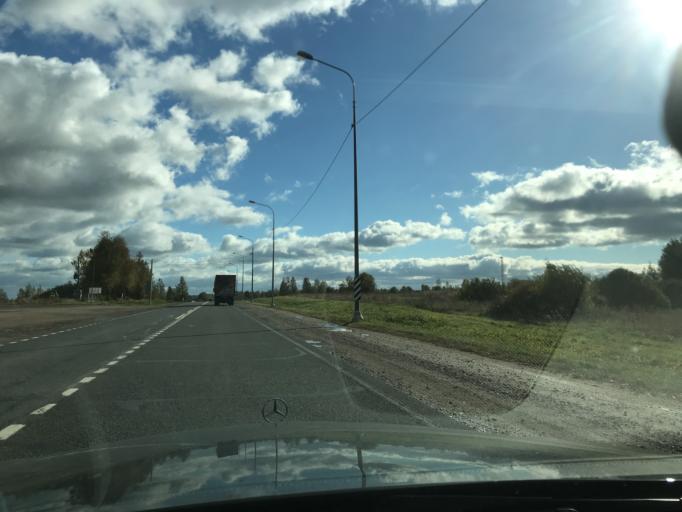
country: RU
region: Pskov
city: Ostrov
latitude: 57.2671
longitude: 28.4103
